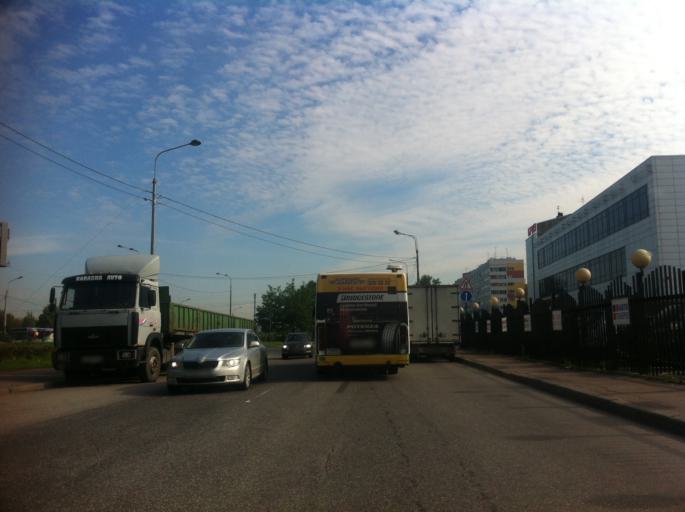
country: RU
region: St.-Petersburg
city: Uritsk
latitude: 59.8269
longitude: 30.1892
